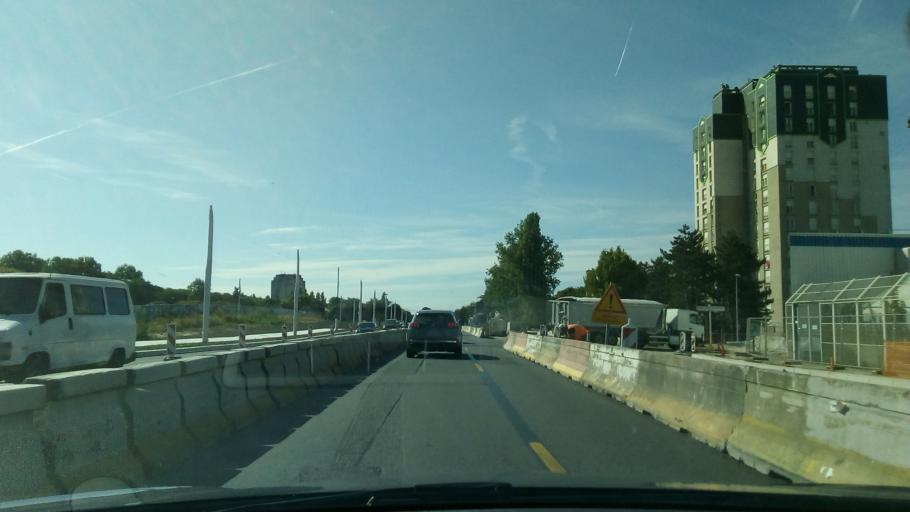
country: FR
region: Ile-de-France
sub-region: Departement de Seine-et-Marne
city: Vert-Saint-Denis
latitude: 48.5565
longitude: 2.6392
